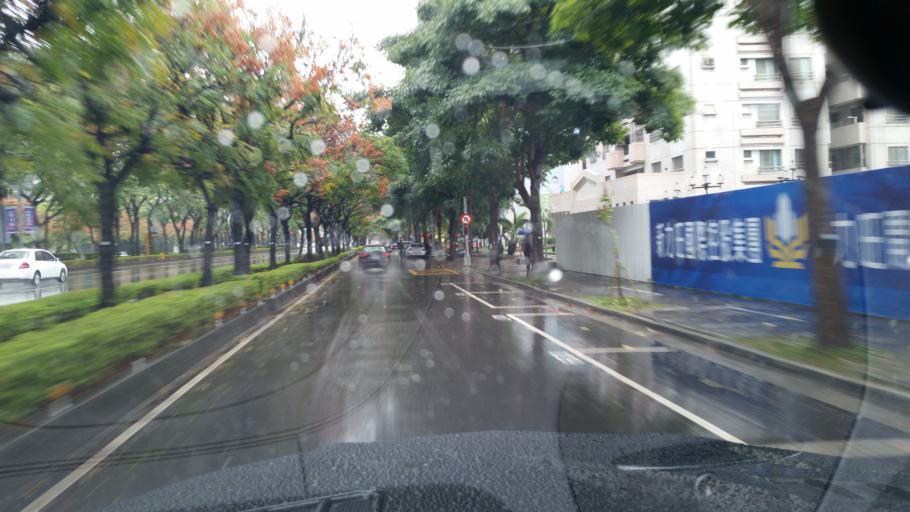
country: TW
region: Taiwan
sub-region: Taichung City
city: Taichung
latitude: 24.1586
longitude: 120.6393
